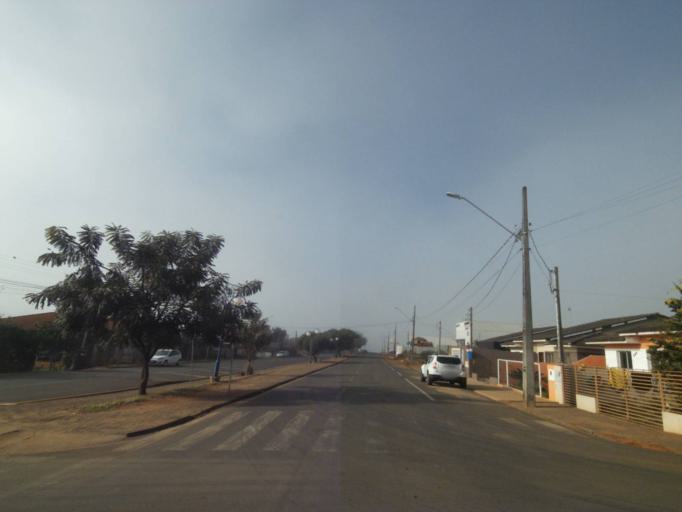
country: BR
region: Parana
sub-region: Tibagi
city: Tibagi
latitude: -24.5228
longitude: -50.4098
